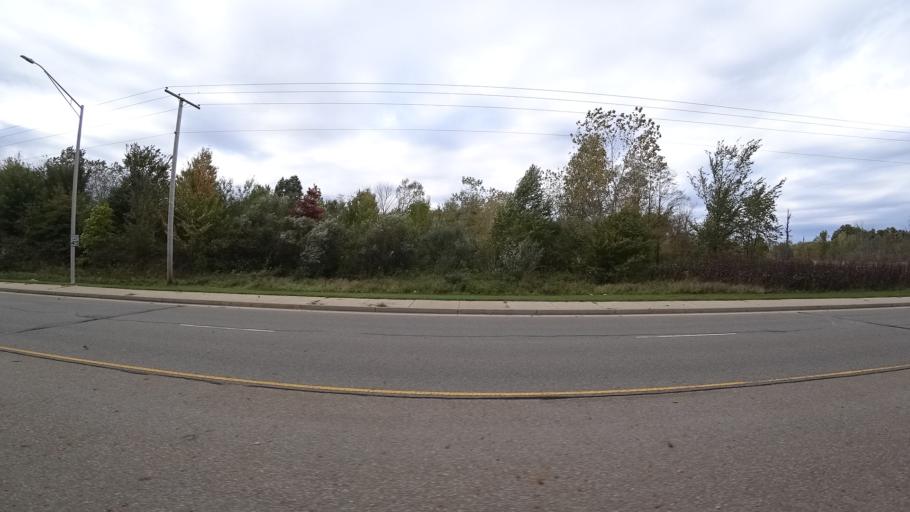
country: US
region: Indiana
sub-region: LaPorte County
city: Trail Creek
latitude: 41.6690
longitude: -86.8845
